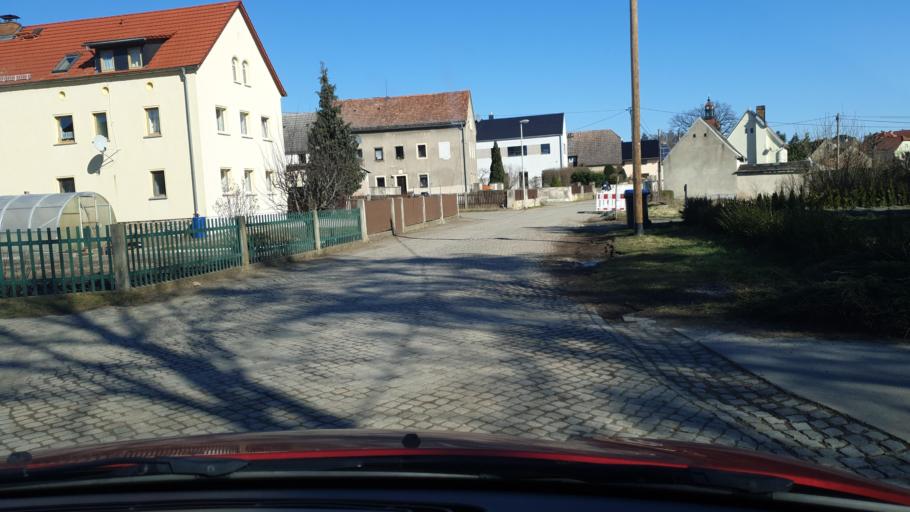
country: DE
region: Saxony
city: Moritzburg
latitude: 51.1549
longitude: 13.6726
